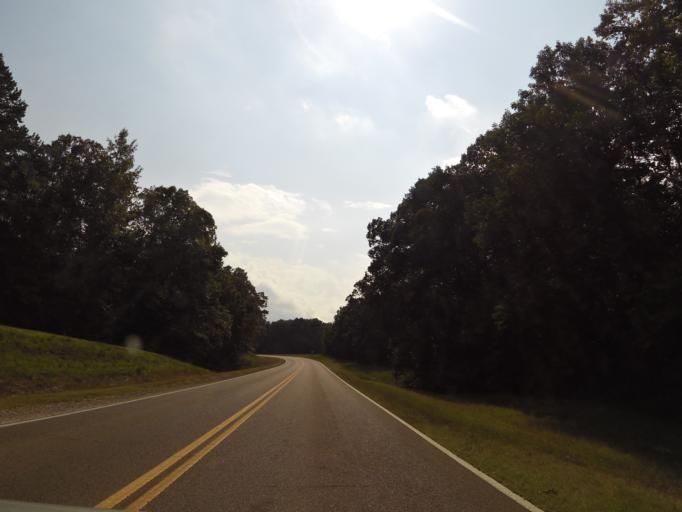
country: US
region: Tennessee
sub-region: Hardin County
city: Crump
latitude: 35.1410
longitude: -88.3572
